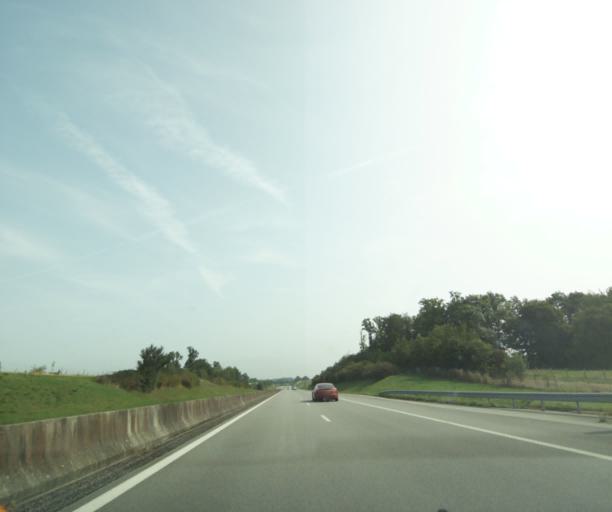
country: FR
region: Lower Normandy
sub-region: Departement de l'Orne
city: Radon
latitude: 48.5216
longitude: 0.1485
